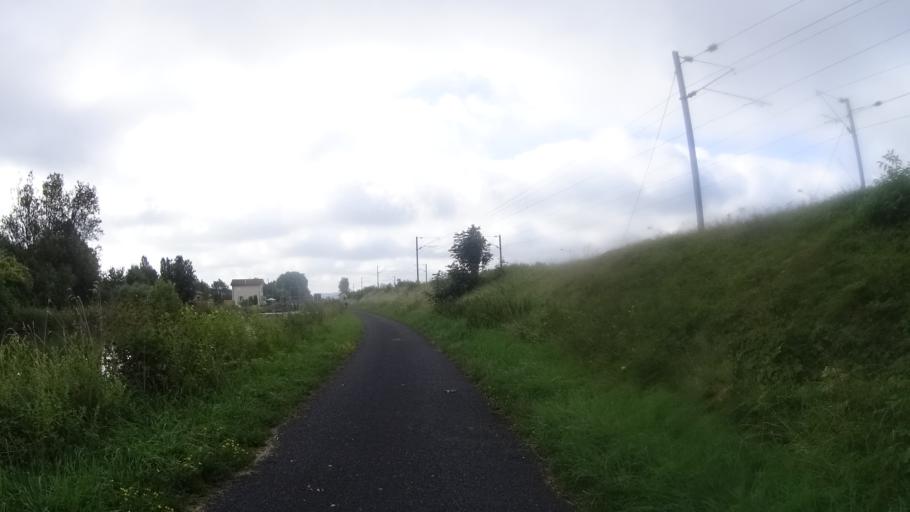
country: FR
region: Lorraine
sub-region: Departement de la Meuse
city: Bar-le-Duc
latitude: 48.7655
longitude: 5.1784
